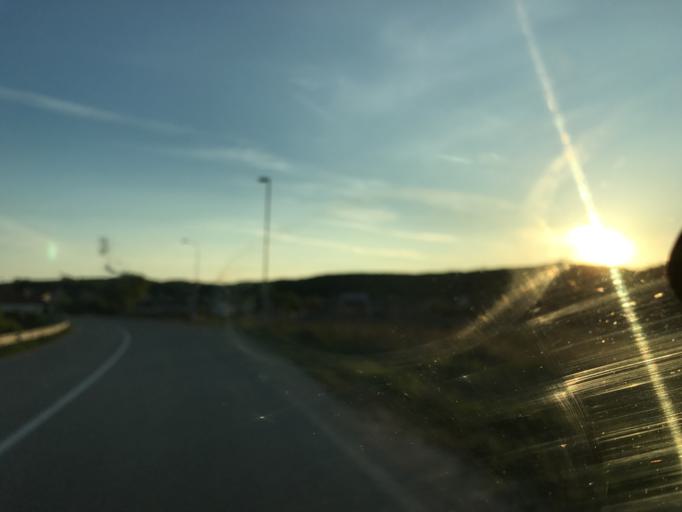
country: RO
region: Mehedinti
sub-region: Comuna Burila Mare
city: Burila Mare
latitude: 44.4867
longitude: 22.4590
